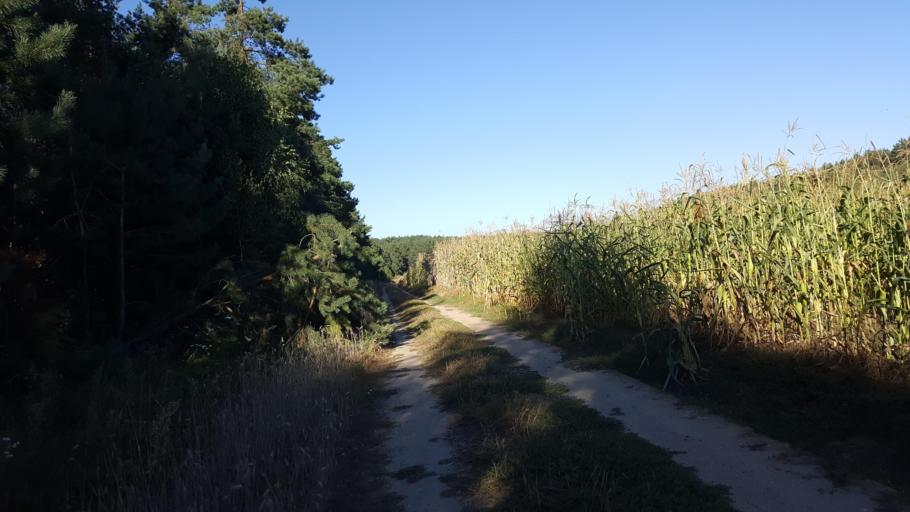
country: PL
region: Lublin Voivodeship
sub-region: Powiat bialski
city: Janow Podlaski
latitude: 52.3058
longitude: 23.2522
